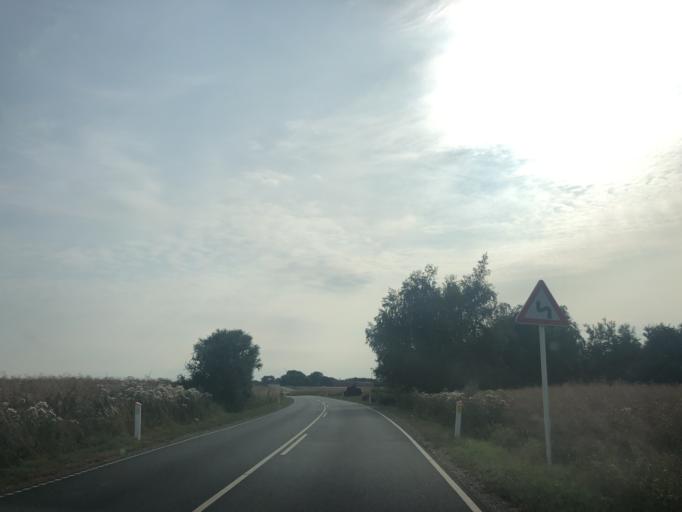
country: DK
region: Central Jutland
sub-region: Skive Kommune
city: Skive
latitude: 56.7082
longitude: 9.0090
